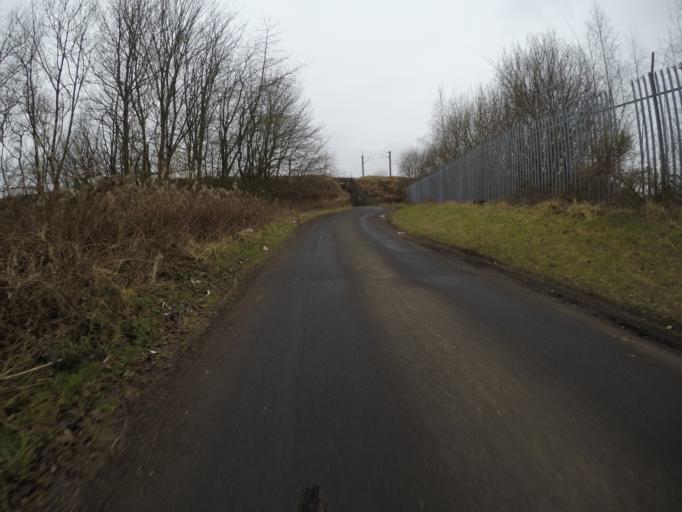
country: GB
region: Scotland
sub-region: North Ayrshire
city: Kilwinning
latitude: 55.6435
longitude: -4.7008
